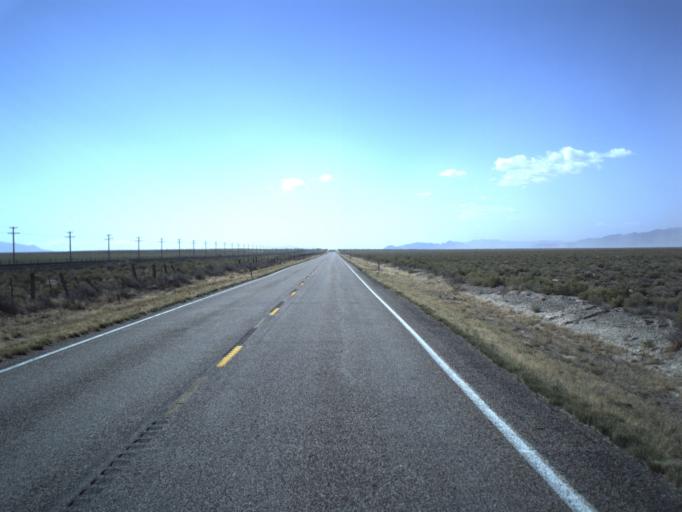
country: US
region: Utah
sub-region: Beaver County
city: Milford
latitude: 38.6981
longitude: -112.9733
